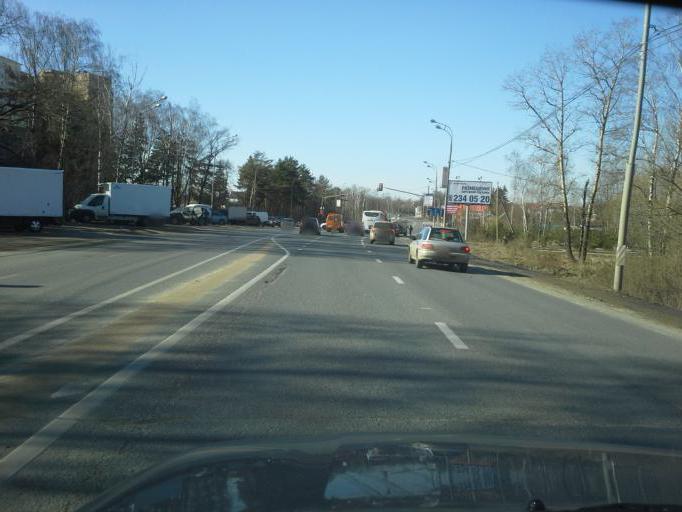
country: RU
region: Moskovskaya
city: Lesnoy Gorodok
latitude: 55.6602
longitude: 37.2005
